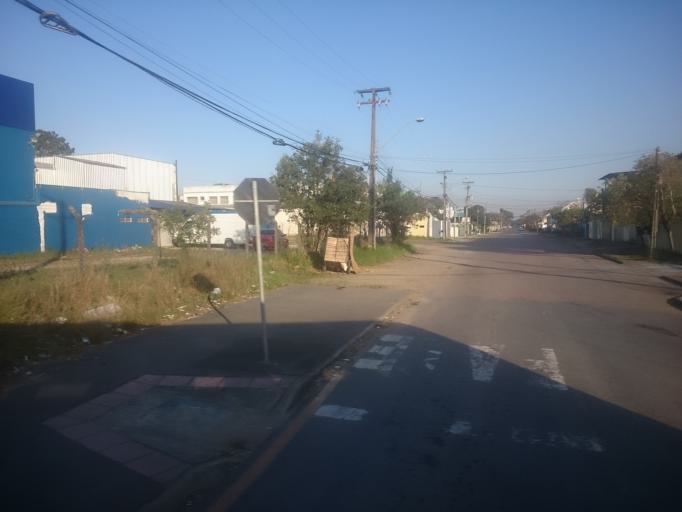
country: BR
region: Parana
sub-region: Curitiba
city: Curitiba
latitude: -25.4733
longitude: -49.2568
